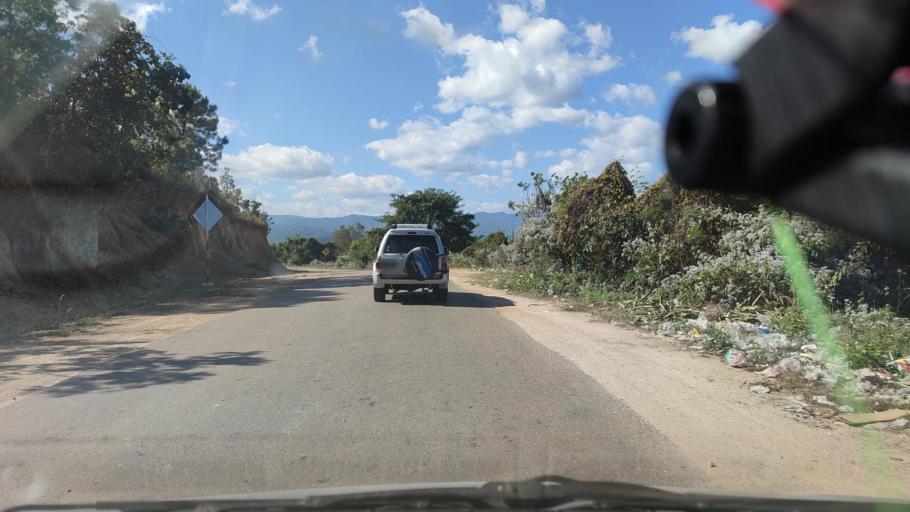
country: MM
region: Shan
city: Taunggyi
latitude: 21.2517
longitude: 97.6471
